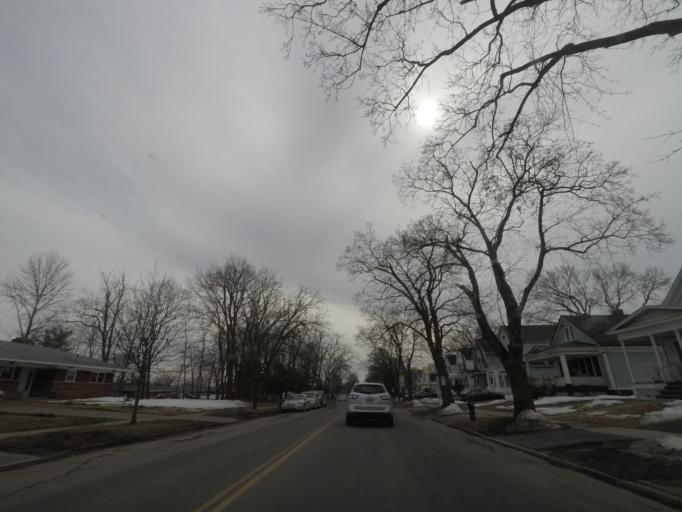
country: US
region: New York
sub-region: Albany County
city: Albany
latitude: 42.6503
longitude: -73.7853
